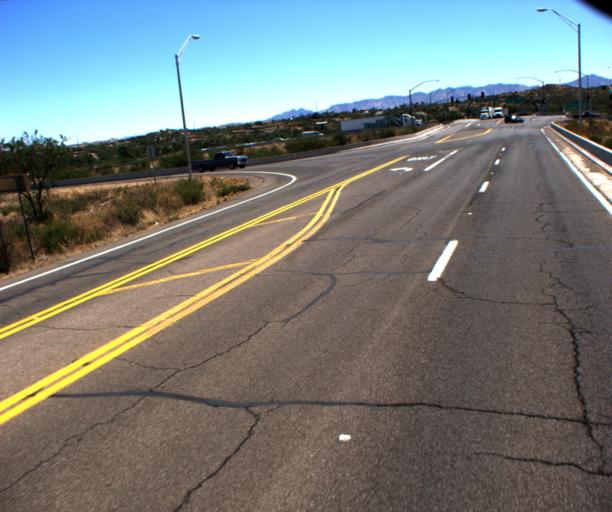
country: US
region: Arizona
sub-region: Santa Cruz County
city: Rio Rico
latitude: 31.4302
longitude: -110.9674
